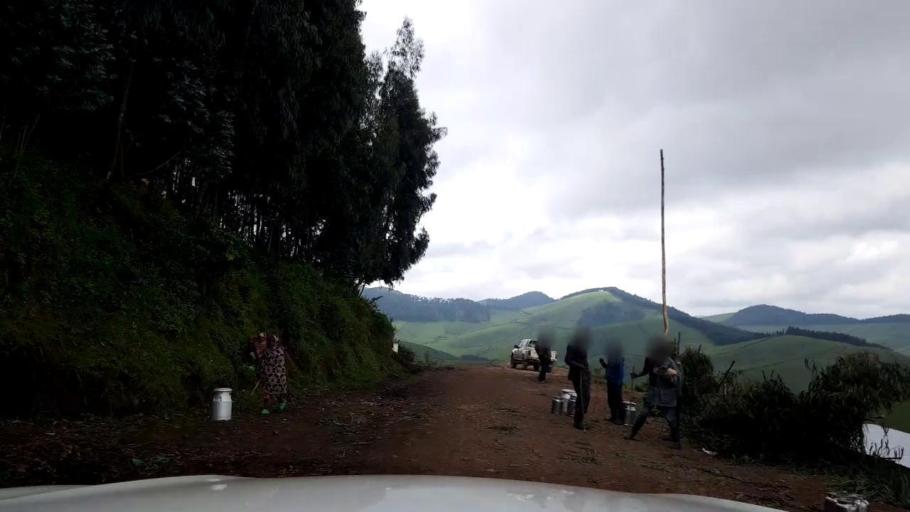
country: RW
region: Western Province
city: Gisenyi
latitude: -1.6767
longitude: 29.4124
